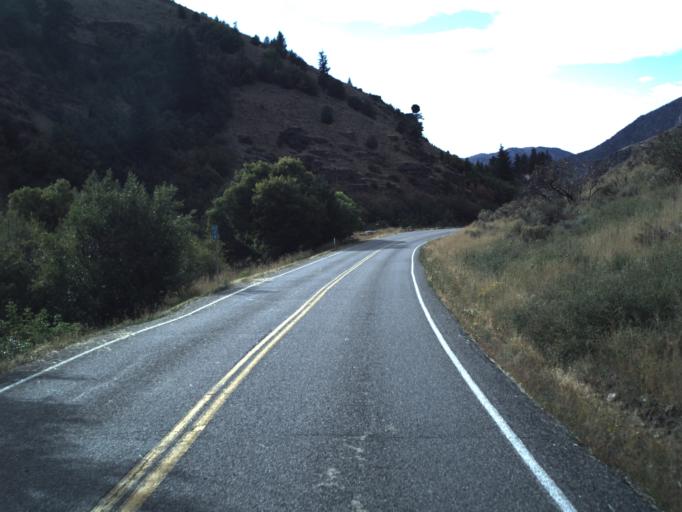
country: US
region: Utah
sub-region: Cache County
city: Millville
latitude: 41.6093
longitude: -111.6252
